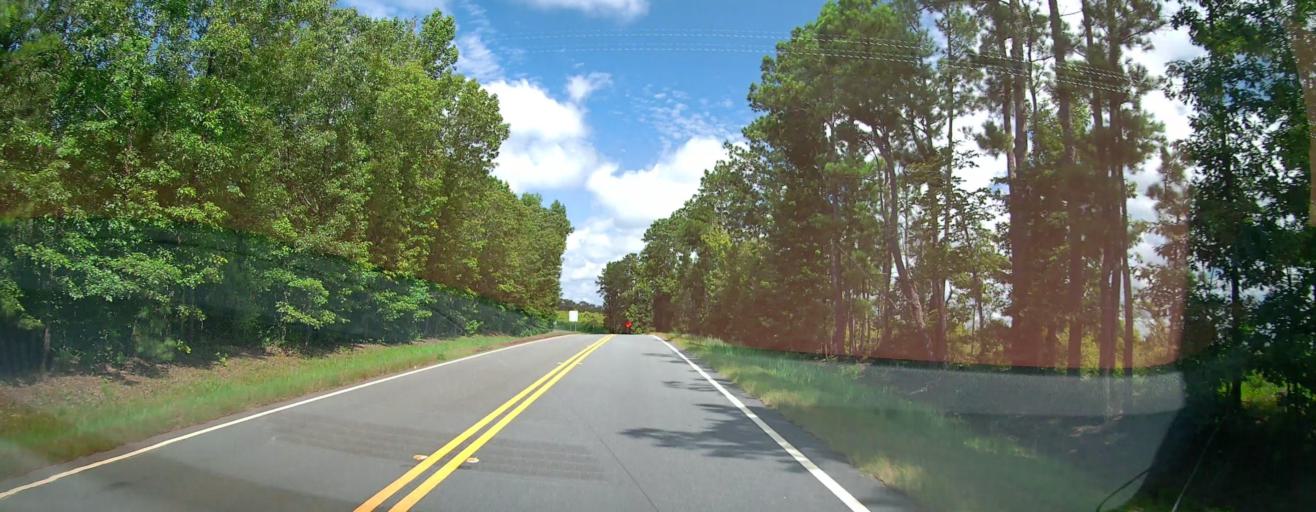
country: US
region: Georgia
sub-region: Crawford County
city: Knoxville
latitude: 32.6789
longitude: -83.9020
